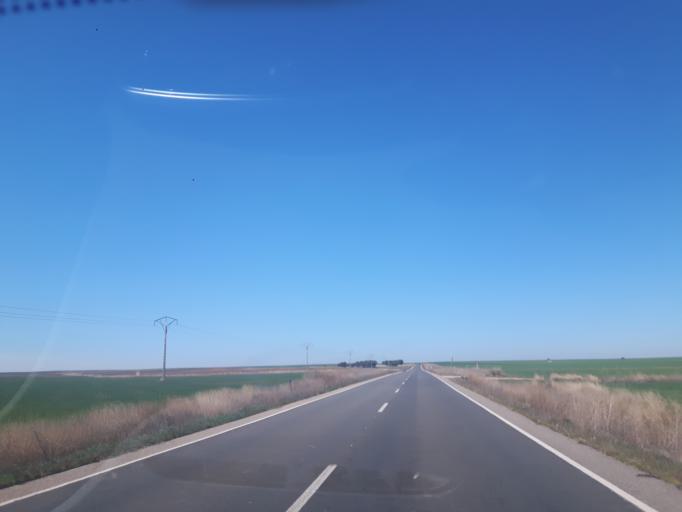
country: ES
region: Castille and Leon
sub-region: Provincia de Salamanca
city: Nava de Sotrobal
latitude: 40.8871
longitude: -5.2921
